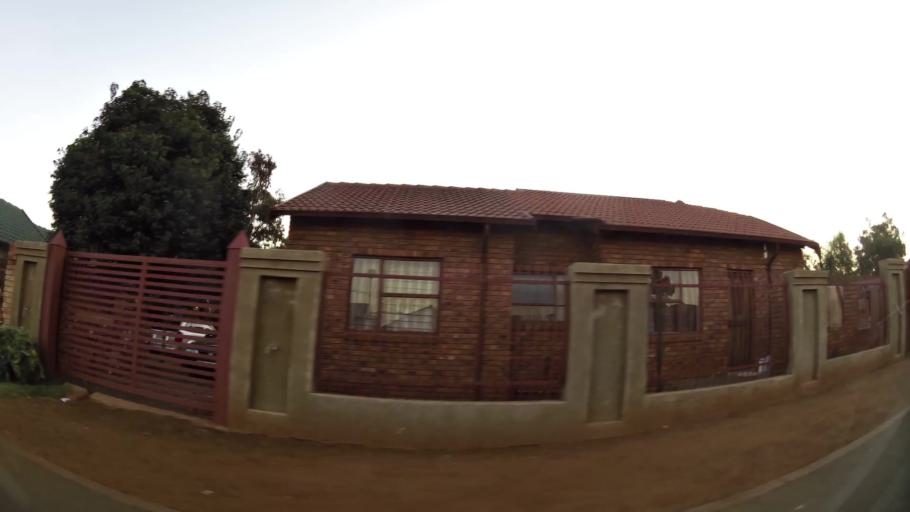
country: ZA
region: Gauteng
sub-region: City of Tshwane Metropolitan Municipality
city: Pretoria
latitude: -25.7396
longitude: 28.1481
